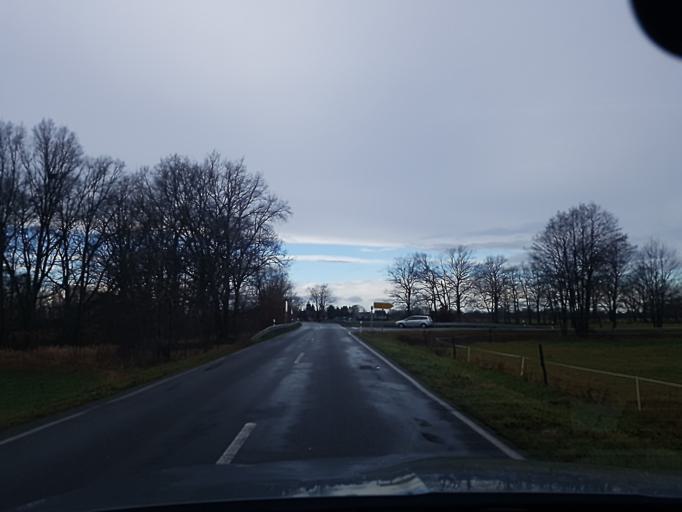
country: DE
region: Brandenburg
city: Schilda
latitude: 51.6073
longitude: 13.3197
